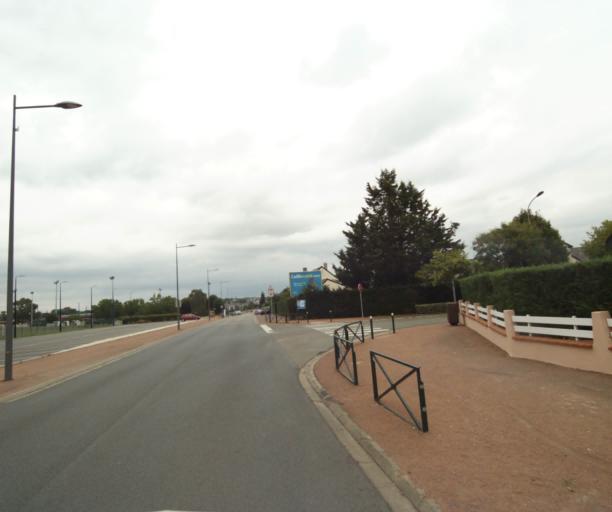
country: FR
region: Pays de la Loire
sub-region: Departement de la Sarthe
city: Sable-sur-Sarthe
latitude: 47.8281
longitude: -0.3195
